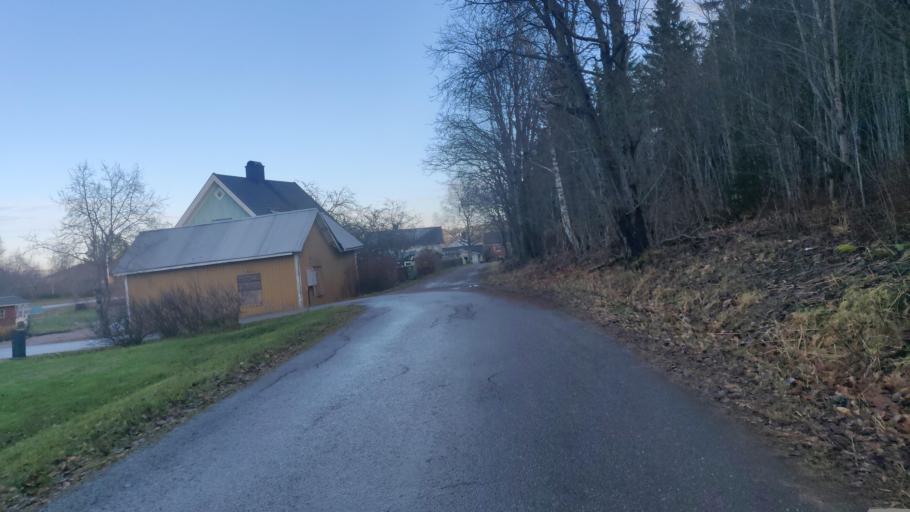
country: SE
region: Vaesternorrland
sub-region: Sundsvalls Kommun
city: Kvissleby
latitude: 62.3101
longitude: 17.3666
